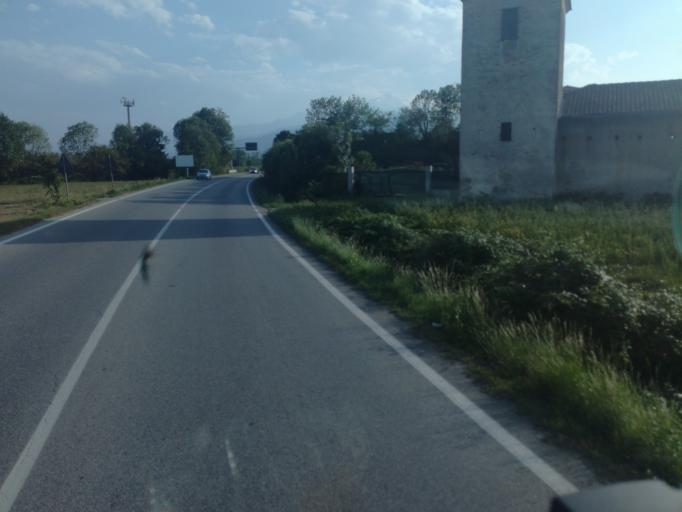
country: IT
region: Piedmont
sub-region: Provincia di Torino
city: Bricherasio
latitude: 44.8246
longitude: 7.3116
